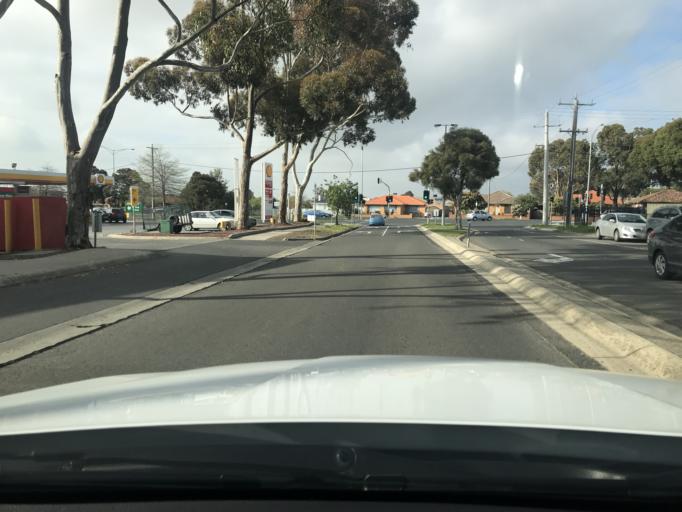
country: AU
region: Victoria
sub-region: Hume
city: Craigieburn
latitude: -37.5978
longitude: 144.9378
